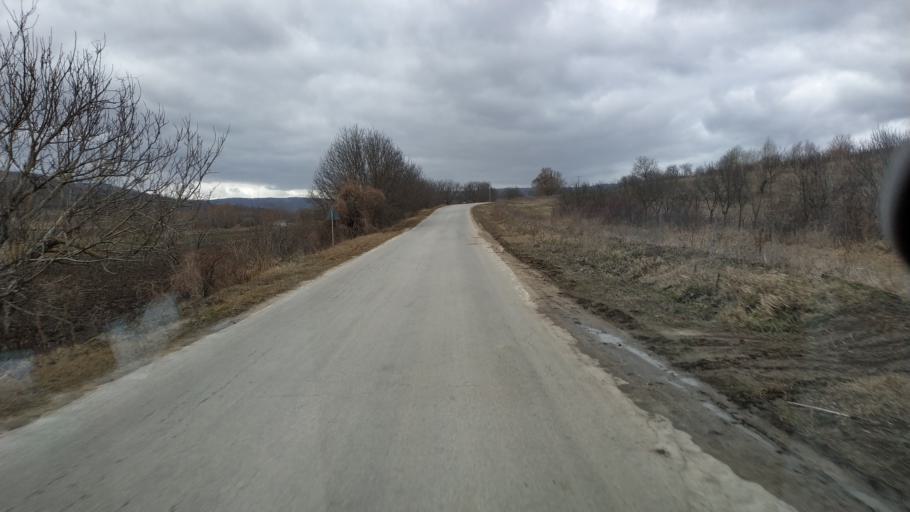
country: MD
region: Calarasi
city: Calarasi
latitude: 47.2431
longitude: 28.1592
